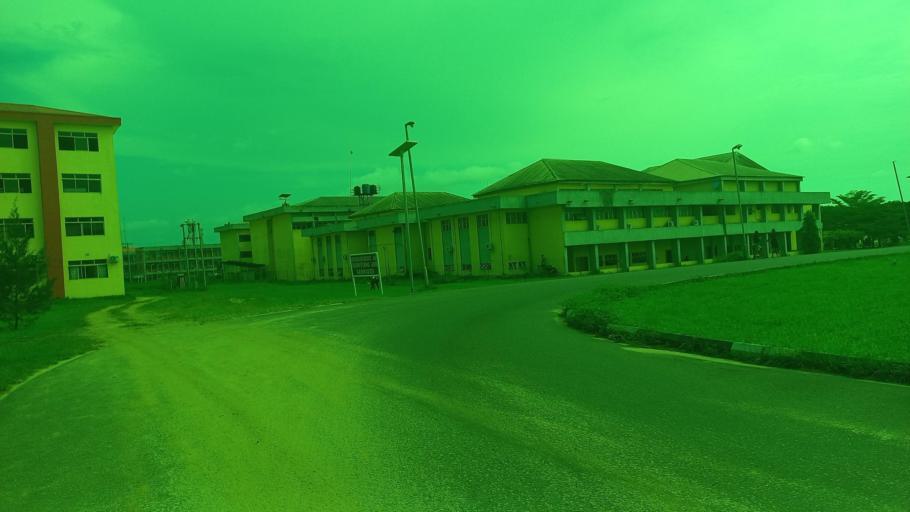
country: NG
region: Rivers
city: Port Harcourt
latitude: 4.8004
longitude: 6.9787
